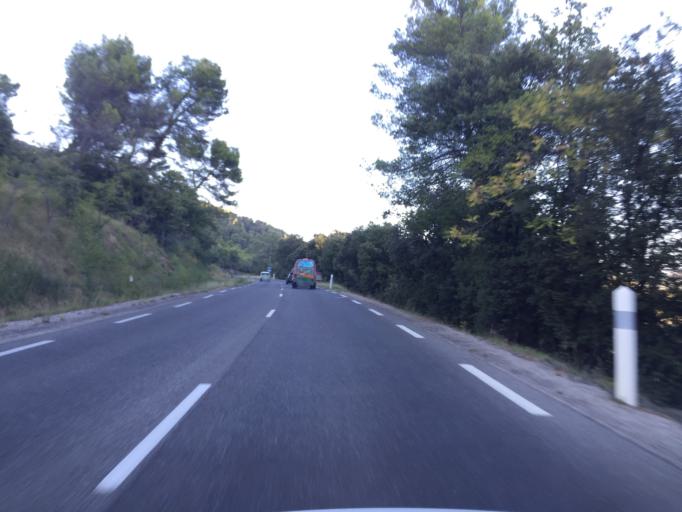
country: FR
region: Provence-Alpes-Cote d'Azur
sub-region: Departement des Alpes-de-Haute-Provence
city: Peyruis
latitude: 43.9847
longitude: 5.9113
